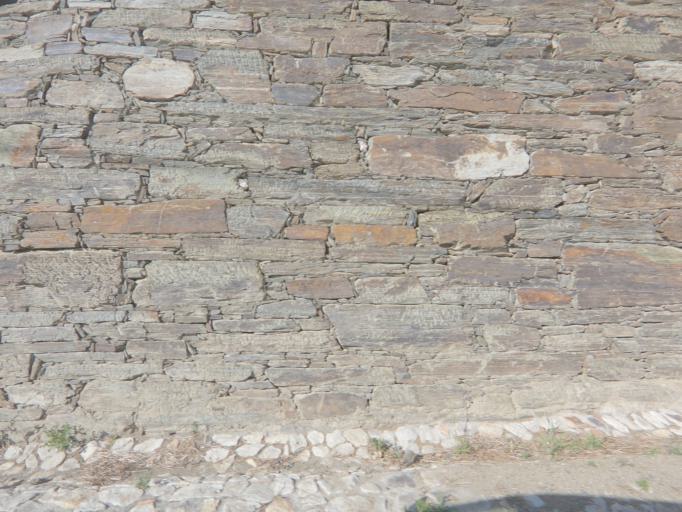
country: PT
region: Vila Real
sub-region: Sabrosa
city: Vilela
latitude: 41.1750
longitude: -7.5780
